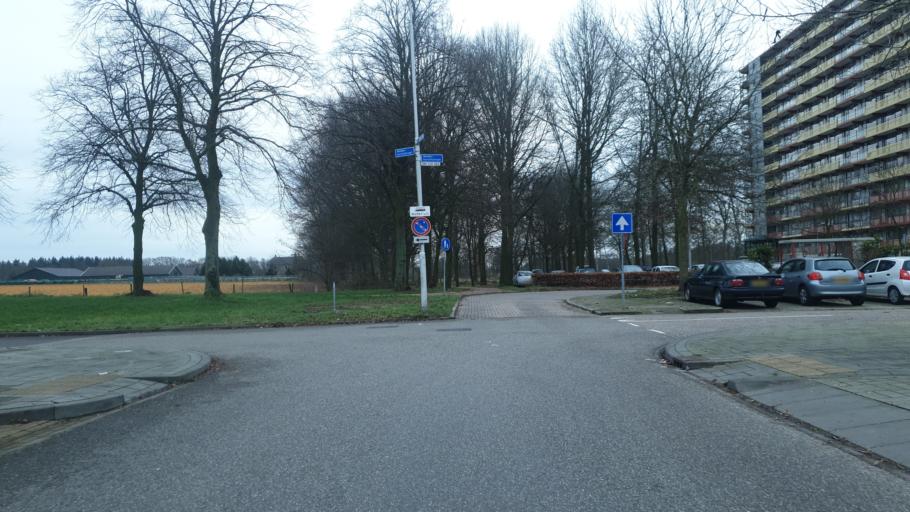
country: NL
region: Gelderland
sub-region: Gemeente Nijmegen
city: Lindenholt
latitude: 51.8004
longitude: 5.8250
